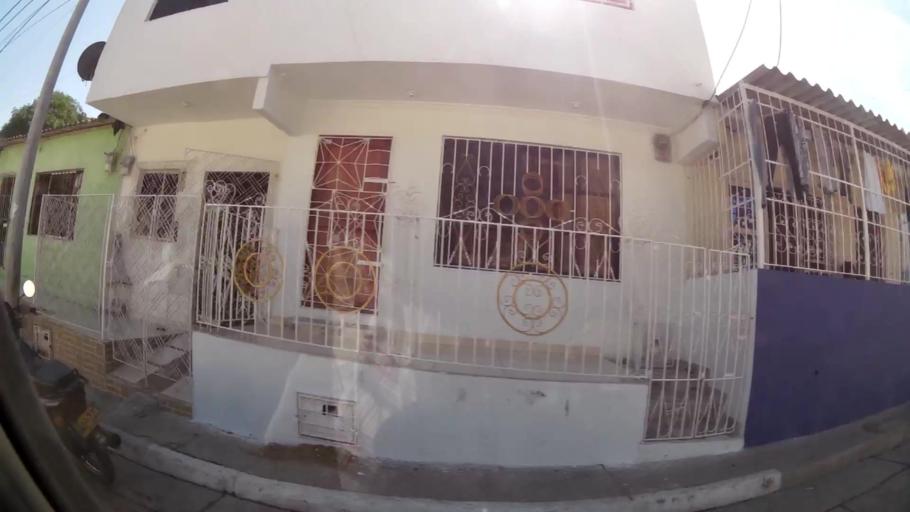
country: CO
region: Bolivar
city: Cartagena
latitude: 10.4359
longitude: -75.5209
